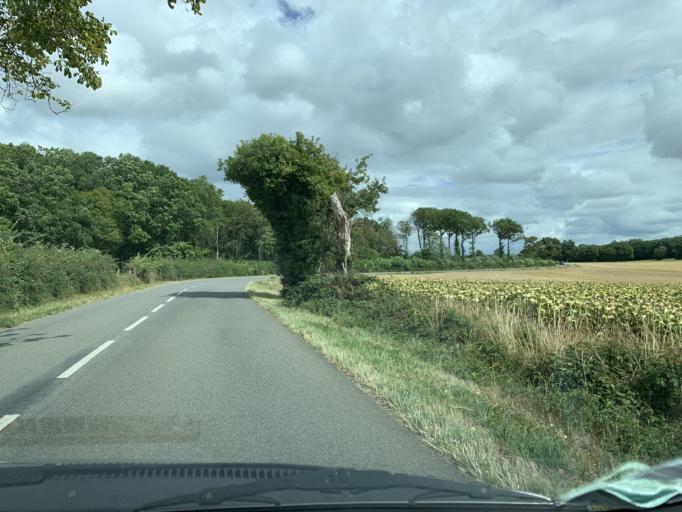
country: FR
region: Bourgogne
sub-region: Departement de la Nievre
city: Clamecy
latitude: 47.4465
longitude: 3.5161
